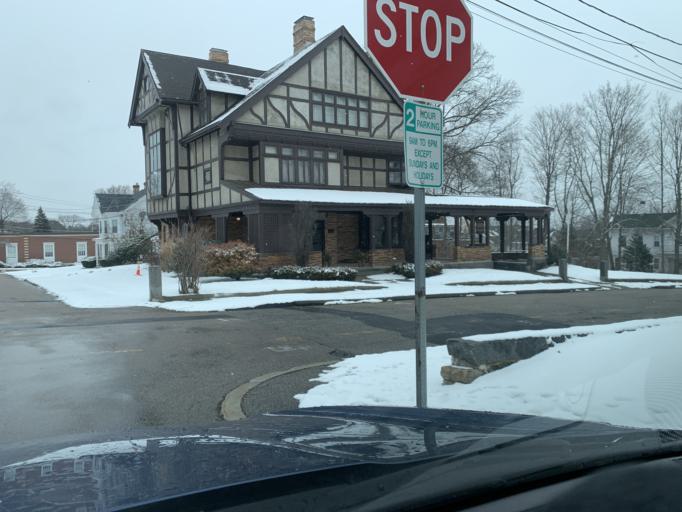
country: US
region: Massachusetts
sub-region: Norfolk County
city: Norwood
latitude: 42.1929
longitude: -71.2037
